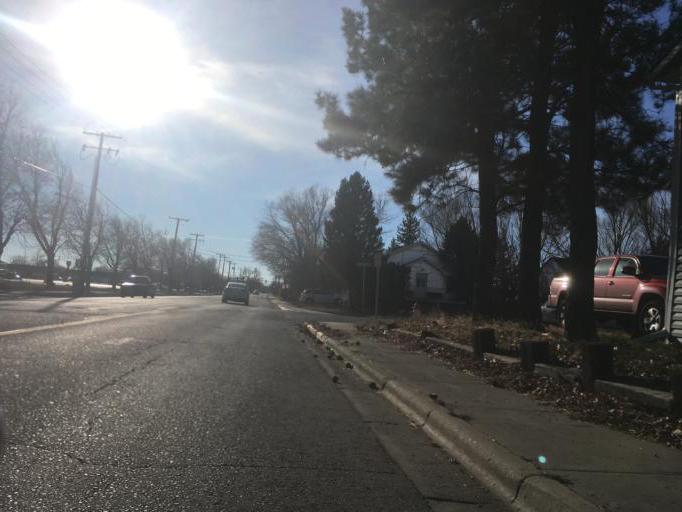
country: US
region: Montana
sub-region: Yellowstone County
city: Billings
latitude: 45.7864
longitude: -108.5591
